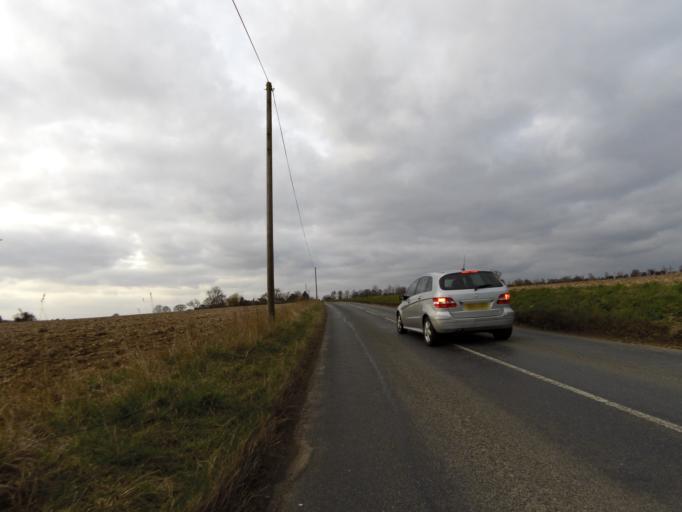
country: GB
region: England
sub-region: Suffolk
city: Ipswich
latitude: 52.1116
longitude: 1.1521
